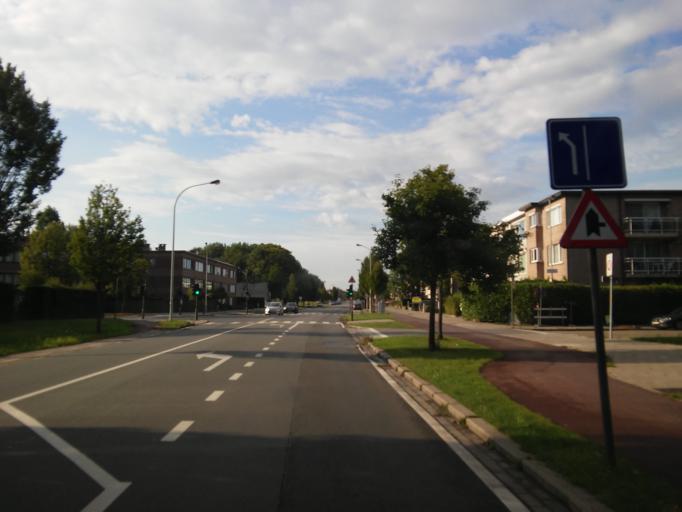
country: BE
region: Flanders
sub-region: Provincie Antwerpen
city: Aartselaar
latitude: 51.1587
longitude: 4.4003
